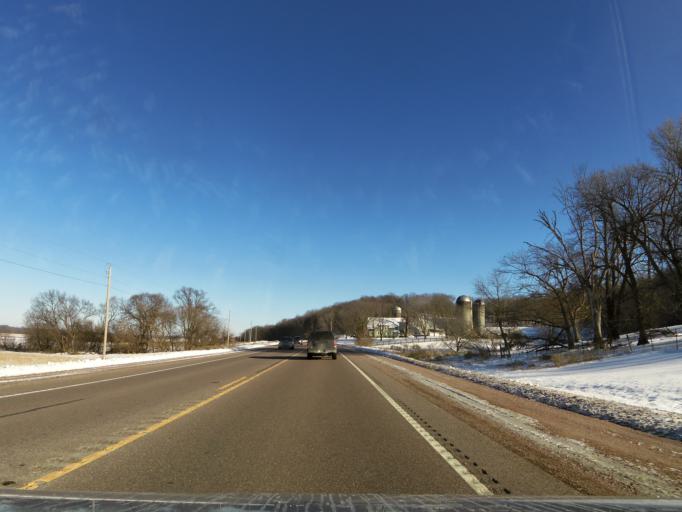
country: US
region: Wisconsin
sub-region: Columbia County
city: Lake Wisconsin
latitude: 43.5035
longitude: -89.6105
